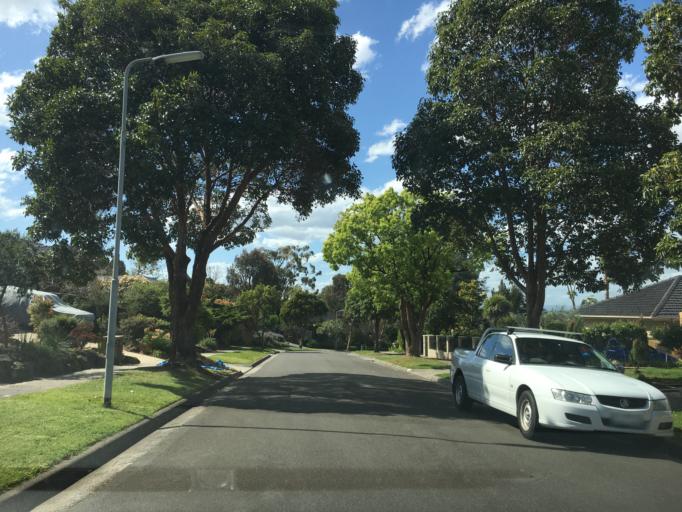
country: AU
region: Victoria
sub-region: Monash
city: Mulgrave
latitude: -37.8943
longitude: 145.1780
